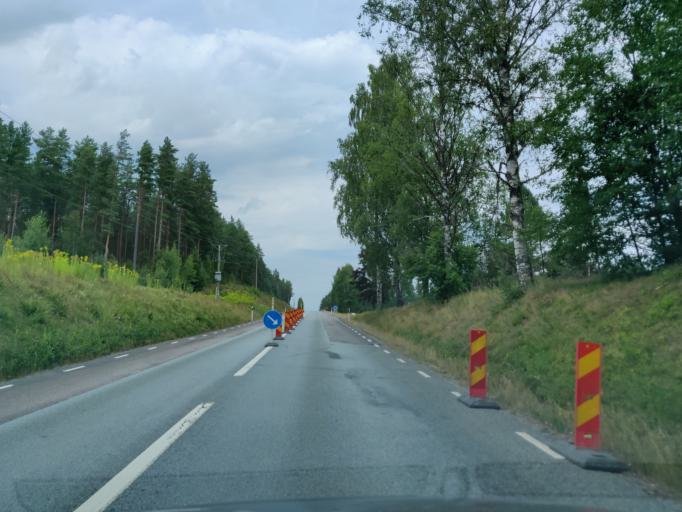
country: SE
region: Vaermland
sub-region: Munkfors Kommun
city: Munkfors
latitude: 59.9149
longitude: 13.5712
